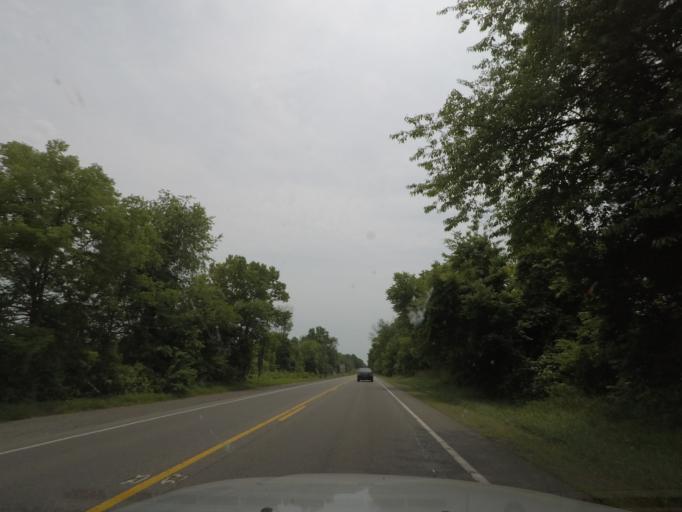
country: US
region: Virginia
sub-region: Prince William County
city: Bull Run Mountain Estates
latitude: 38.9610
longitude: -77.6225
